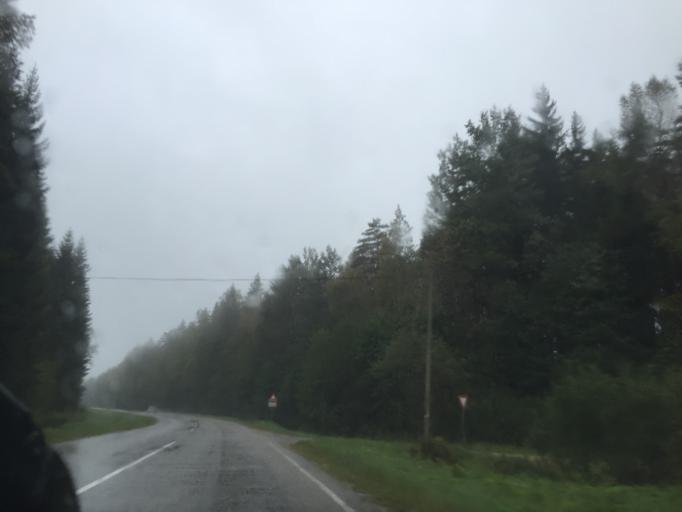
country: LV
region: Ropazu
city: Ropazi
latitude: 56.9969
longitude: 24.6472
